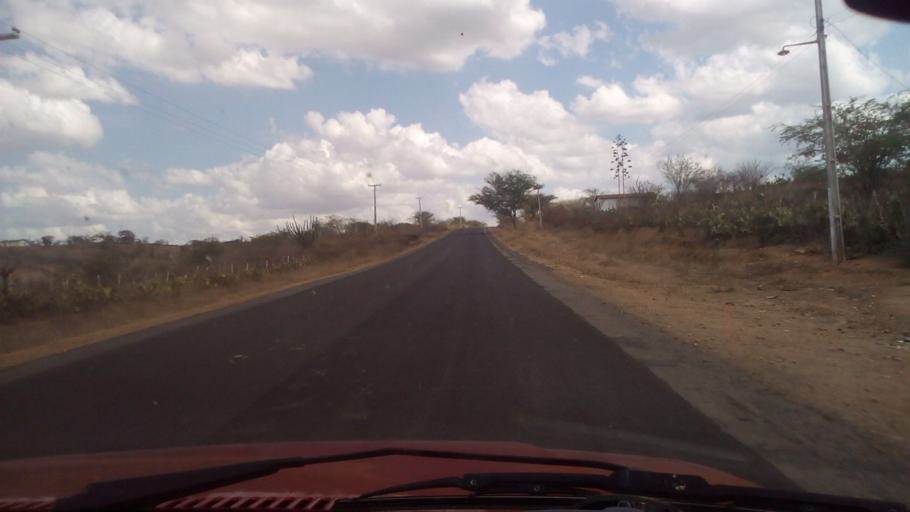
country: BR
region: Paraiba
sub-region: Cacimba De Dentro
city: Cacimba de Dentro
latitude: -6.7098
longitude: -35.7249
